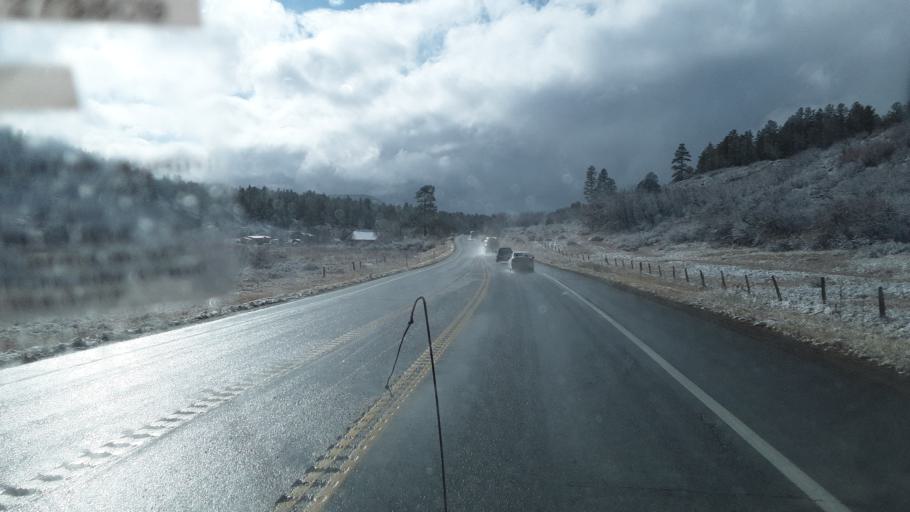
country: US
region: Colorado
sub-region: Archuleta County
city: Pagosa Springs
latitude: 37.2406
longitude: -107.1500
